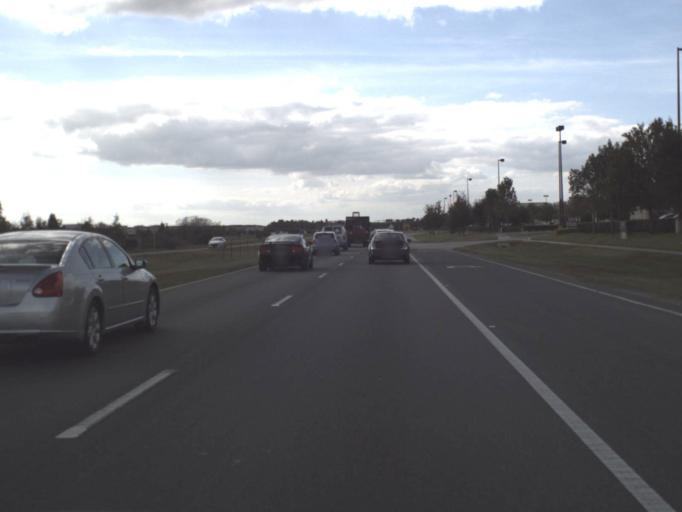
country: US
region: Florida
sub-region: Orange County
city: Hunters Creek
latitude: 28.3423
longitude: -81.4256
